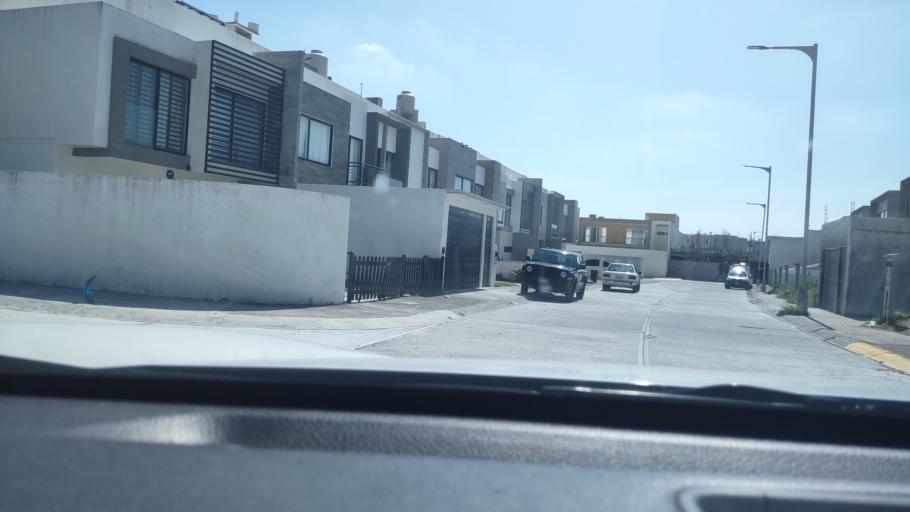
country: MX
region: Veracruz
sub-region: Veracruz
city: Fraccionamiento Geovillas los Pinos
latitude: 19.2204
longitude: -96.2339
